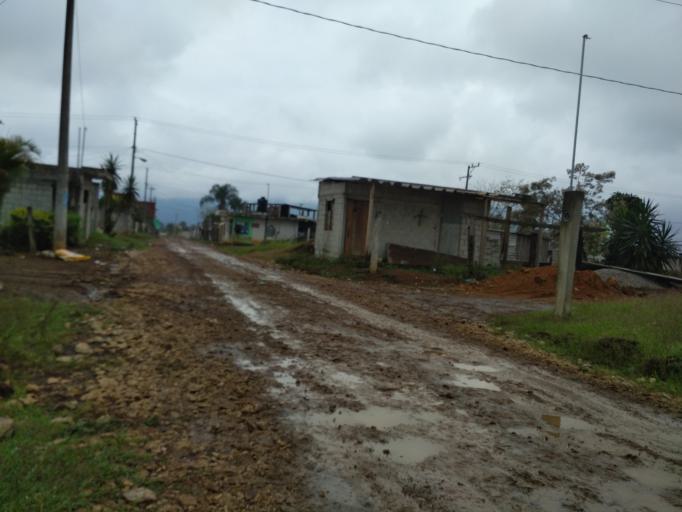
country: MX
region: Veracruz
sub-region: Cordoba
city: San Jose de Tapia
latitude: 18.8501
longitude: -96.9673
